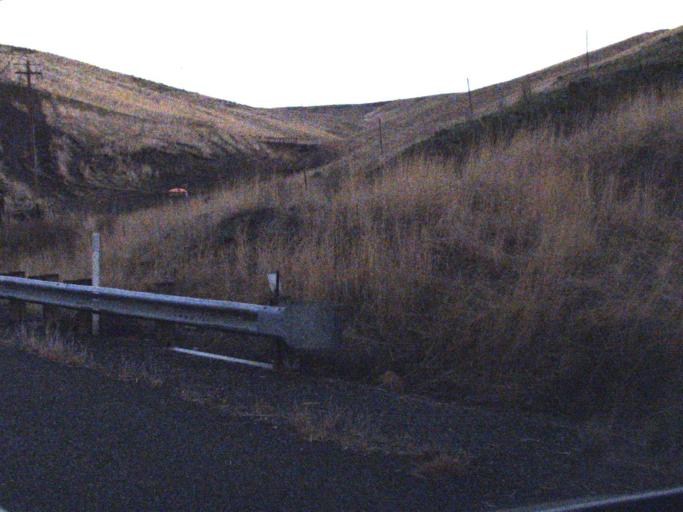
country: US
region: Washington
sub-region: Garfield County
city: Pomeroy
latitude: 46.6015
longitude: -117.7845
